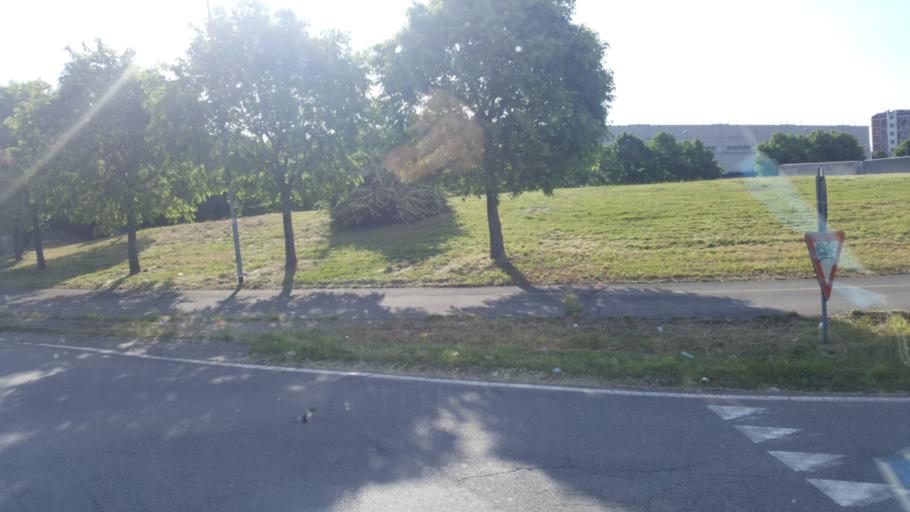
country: IT
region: Lombardy
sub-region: Citta metropolitana di Milano
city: Liscate
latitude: 45.4867
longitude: 9.4092
